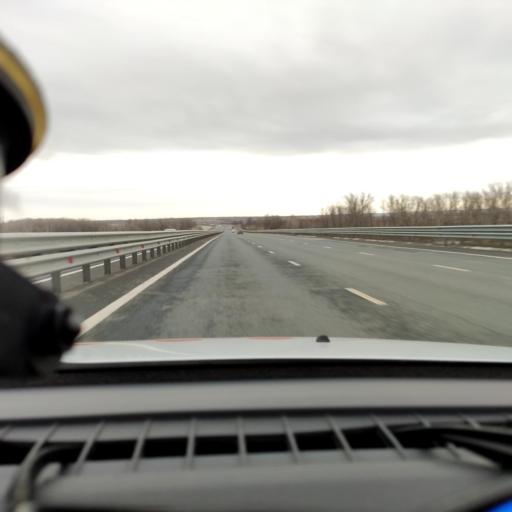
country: RU
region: Samara
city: Smyshlyayevka
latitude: 53.1760
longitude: 50.3102
